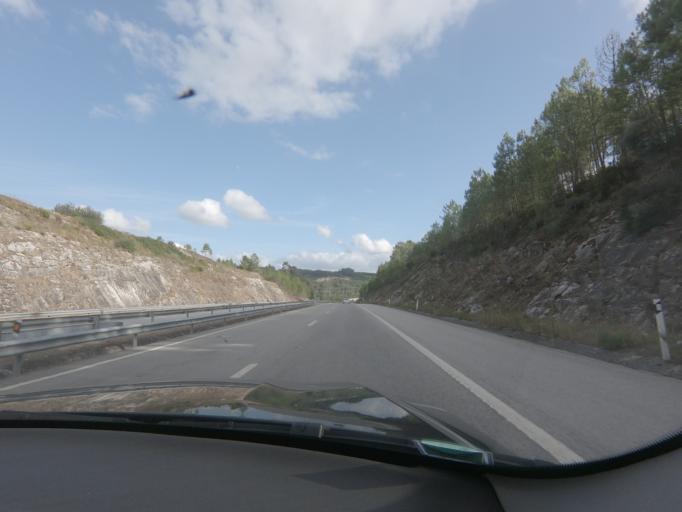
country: PT
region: Viseu
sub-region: Castro Daire
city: Castro Daire
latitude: 40.8303
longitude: -7.9372
